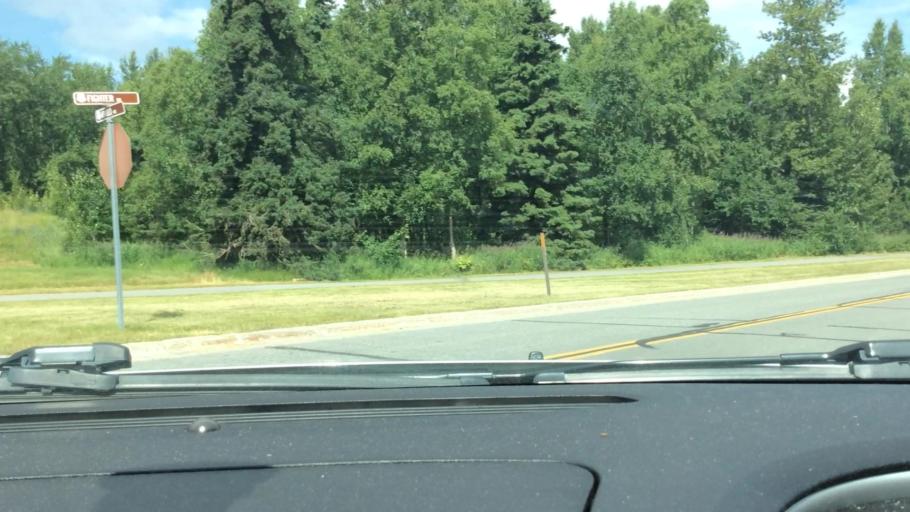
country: US
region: Alaska
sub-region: Anchorage Municipality
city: Anchorage
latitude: 61.2365
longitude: -149.8696
